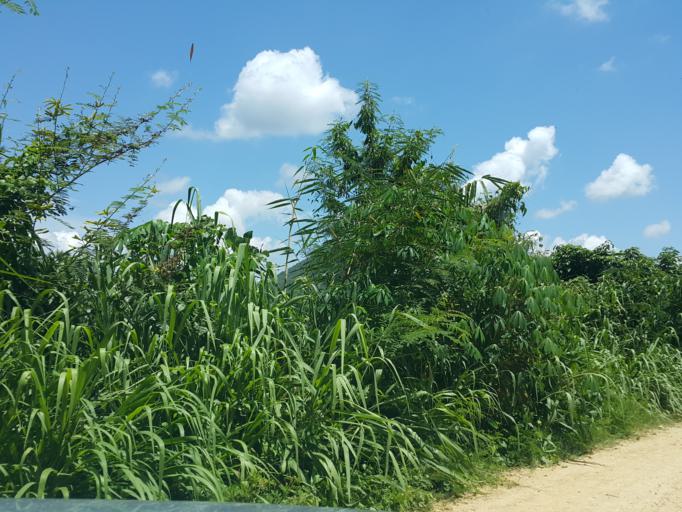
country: TH
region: Lamphun
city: Ban Thi
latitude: 18.6637
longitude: 99.1695
